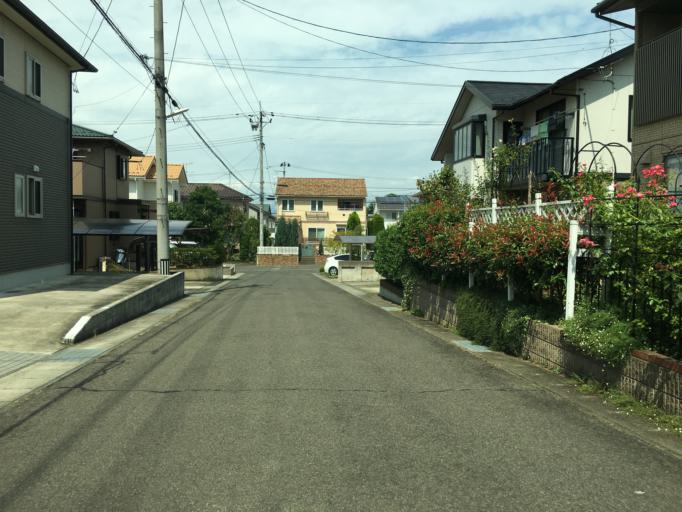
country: JP
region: Fukushima
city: Fukushima-shi
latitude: 37.7118
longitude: 140.4734
